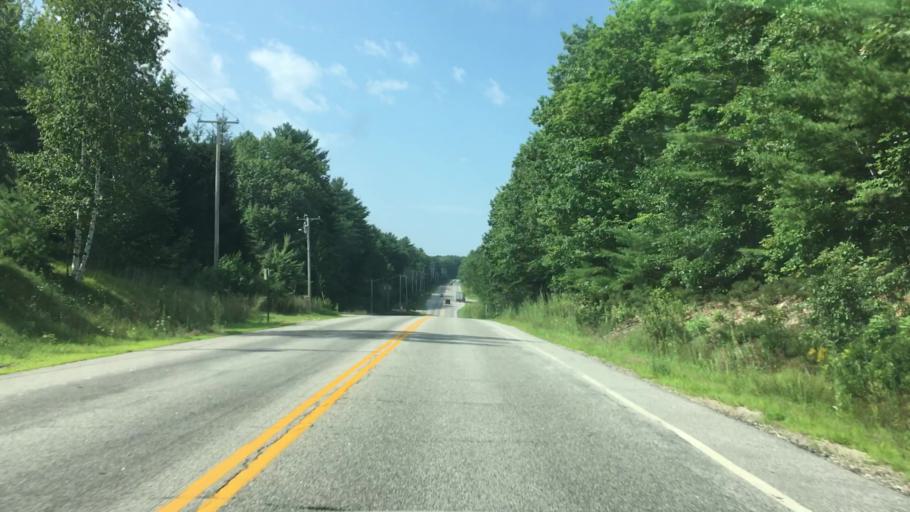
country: US
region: Maine
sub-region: Androscoggin County
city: Poland
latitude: 44.0268
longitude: -70.3479
